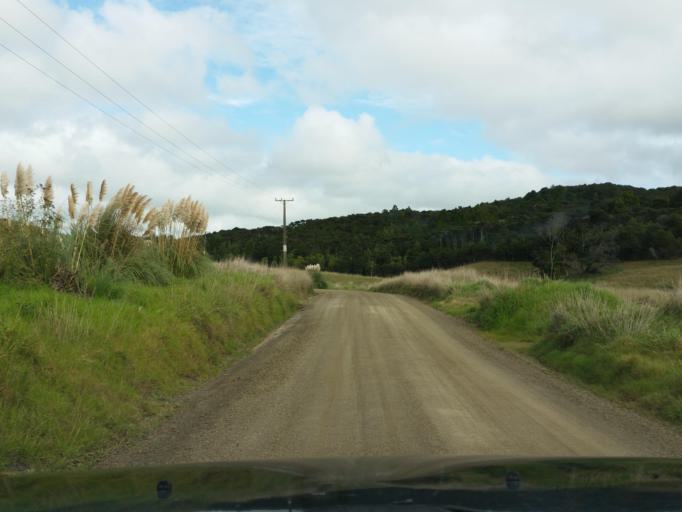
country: NZ
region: Northland
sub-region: Kaipara District
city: Dargaville
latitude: -36.1146
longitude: 174.1327
